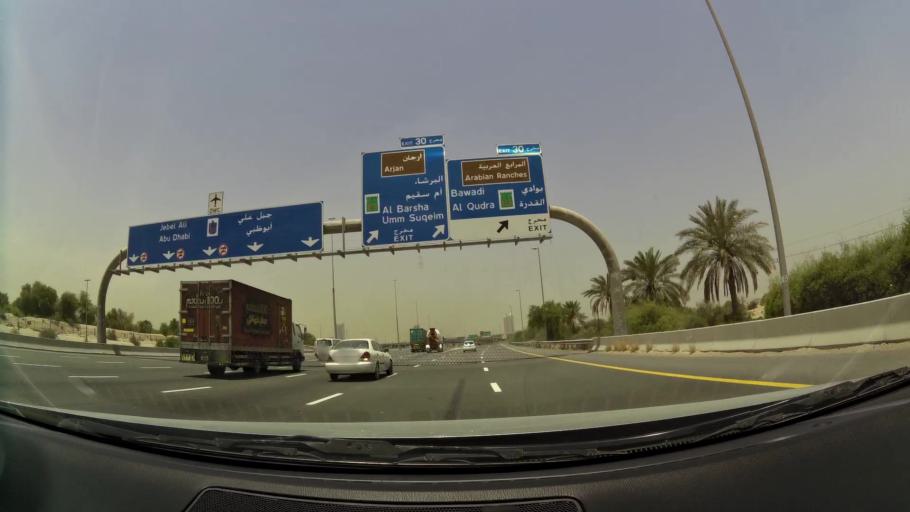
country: AE
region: Dubai
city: Dubai
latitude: 25.0571
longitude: 55.2573
